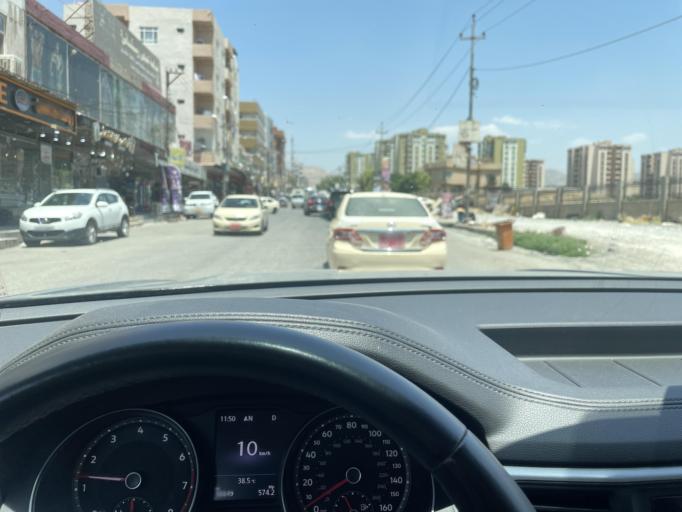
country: IQ
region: Dahuk
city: Saymayl
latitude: 36.8585
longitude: 42.9053
